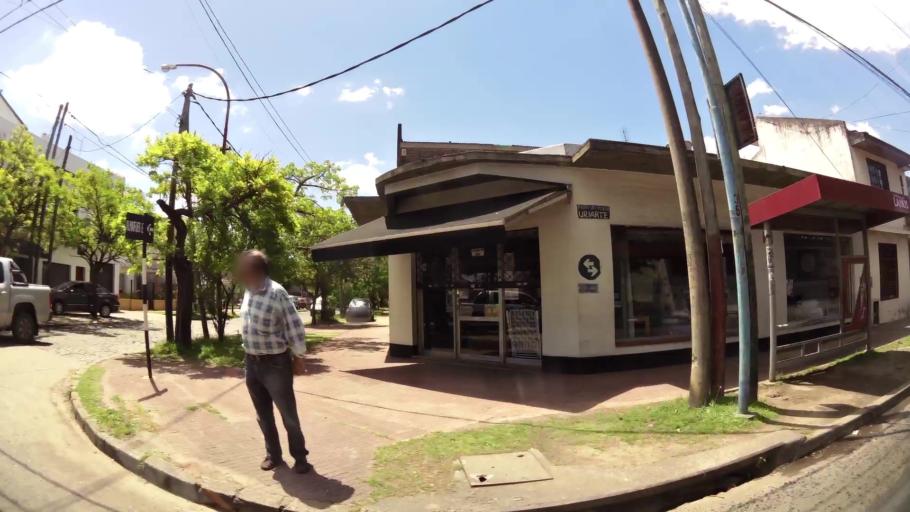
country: AR
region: Buenos Aires
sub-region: Partido de Lomas de Zamora
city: Lomas de Zamora
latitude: -34.7337
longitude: -58.4072
